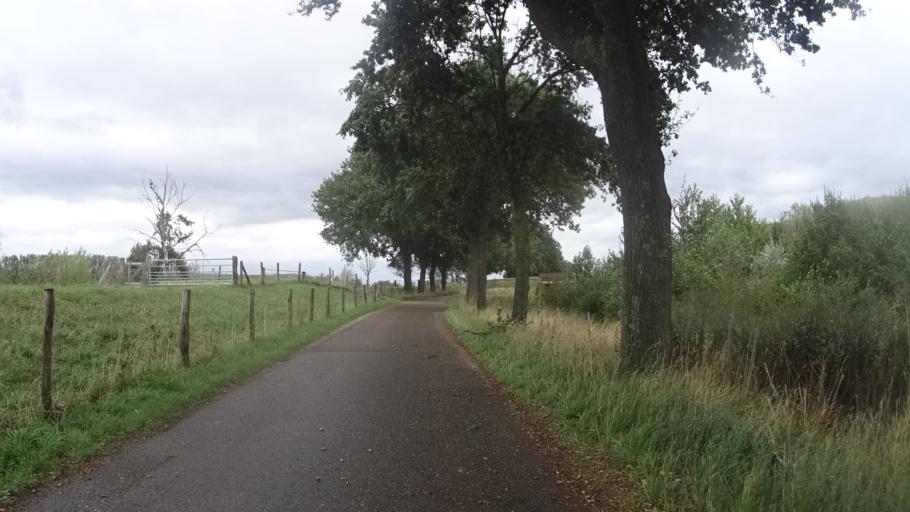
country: NL
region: Limburg
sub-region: Gemeente Sittard-Geleen
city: Born
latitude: 51.0500
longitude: 5.7897
